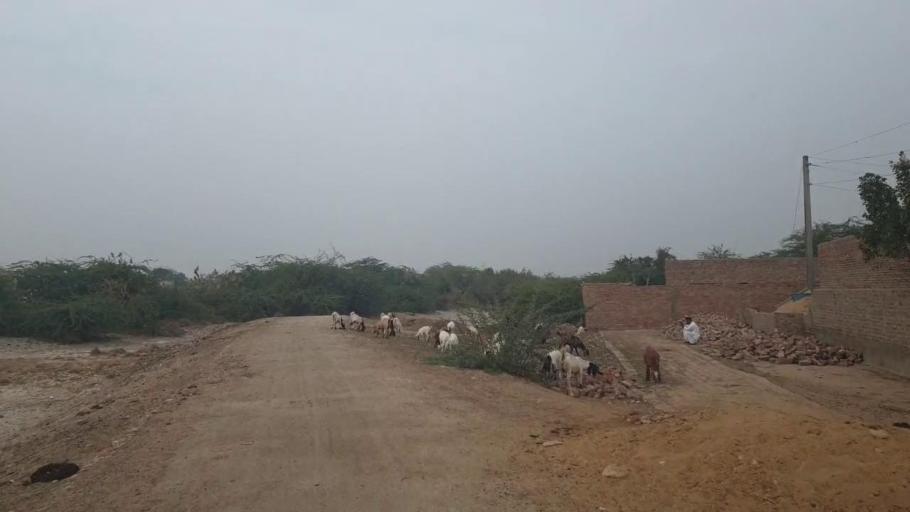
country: PK
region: Sindh
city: Berani
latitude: 25.8097
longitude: 68.7341
